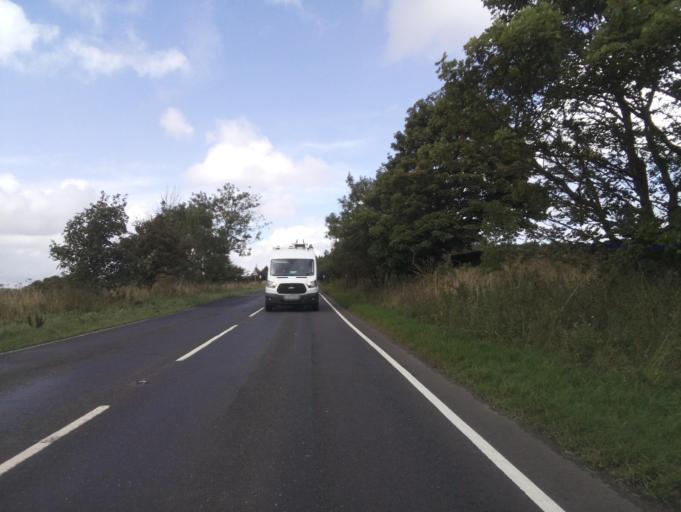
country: GB
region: England
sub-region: County Durham
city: Muggleswick
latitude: 54.8577
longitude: -1.9216
